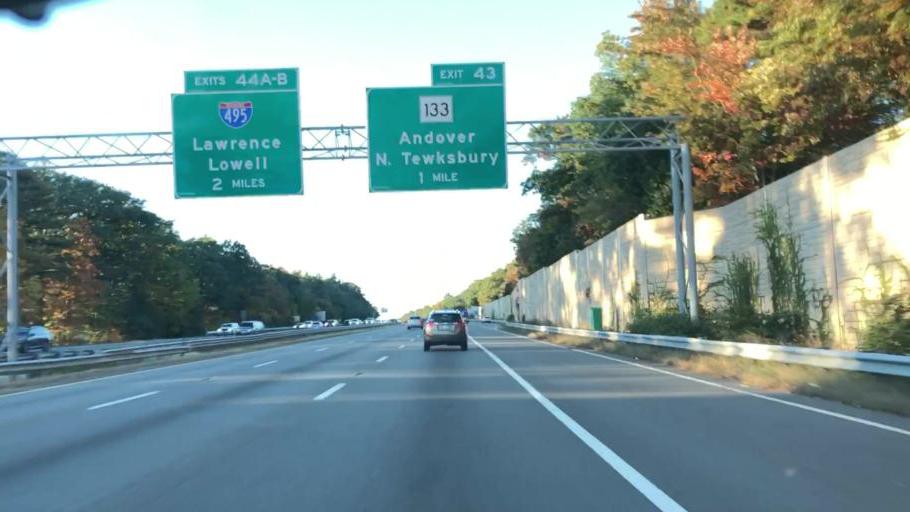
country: US
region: Massachusetts
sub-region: Essex County
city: Andover
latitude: 42.6295
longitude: -71.1790
